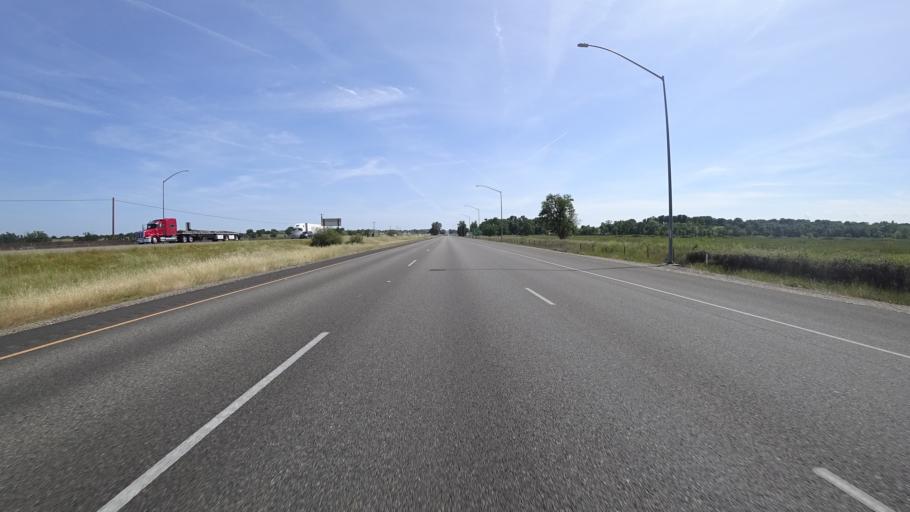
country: US
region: California
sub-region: Shasta County
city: Cottonwood
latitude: 40.3648
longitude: -122.2841
